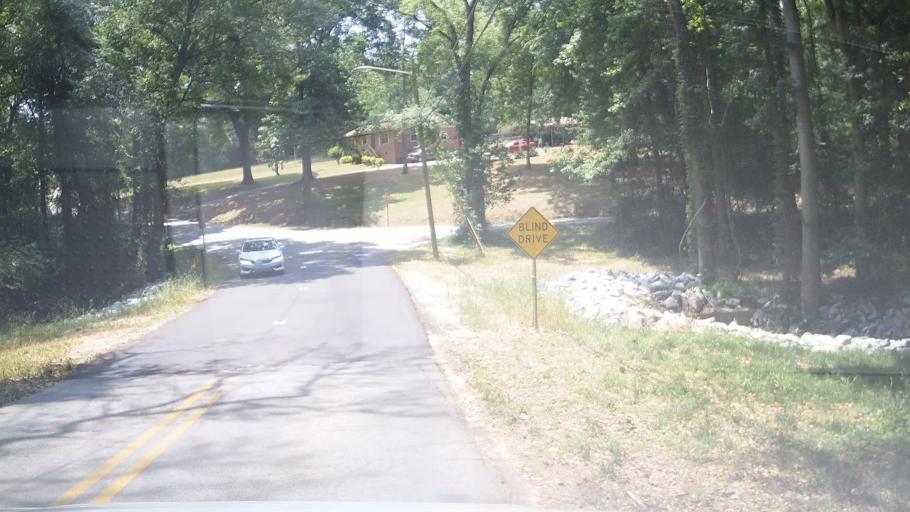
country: US
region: Georgia
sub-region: Hart County
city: Hartwell
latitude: 34.3471
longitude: -82.9345
